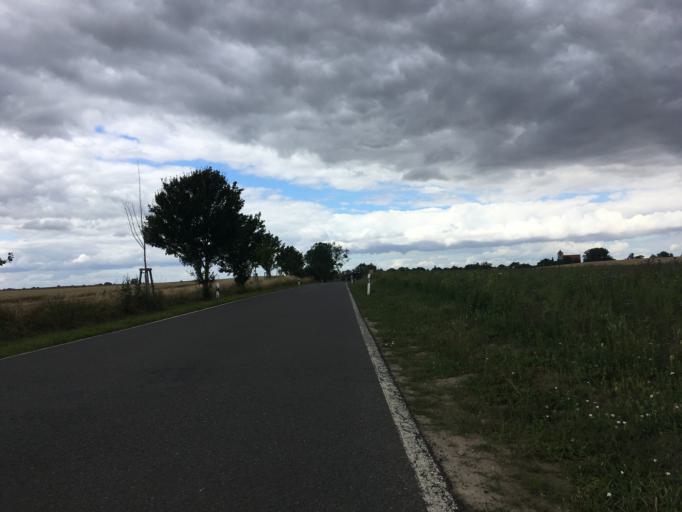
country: DE
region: Brandenburg
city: Gramzow
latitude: 53.2370
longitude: 13.9416
